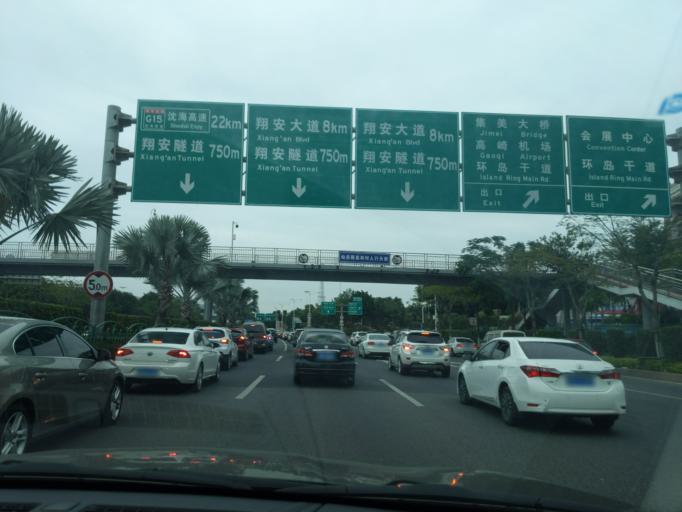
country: CN
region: Fujian
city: Liuwudian
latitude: 24.5122
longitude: 118.1773
